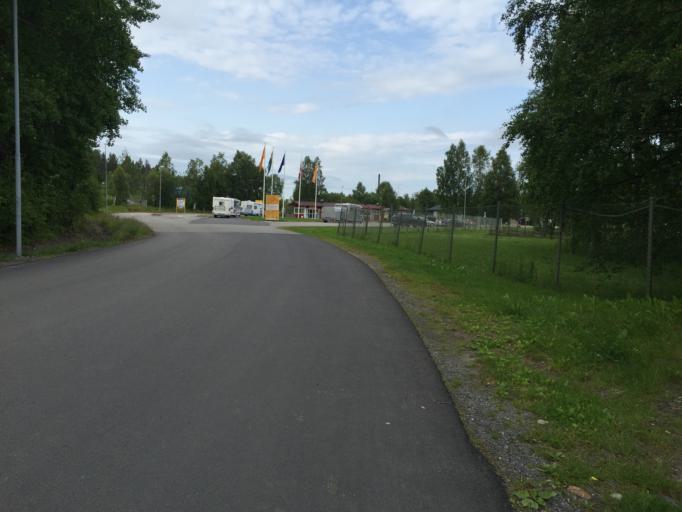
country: SE
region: Vaesterbotten
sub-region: Umea Kommun
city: Ersmark
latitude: 63.8421
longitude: 20.3401
